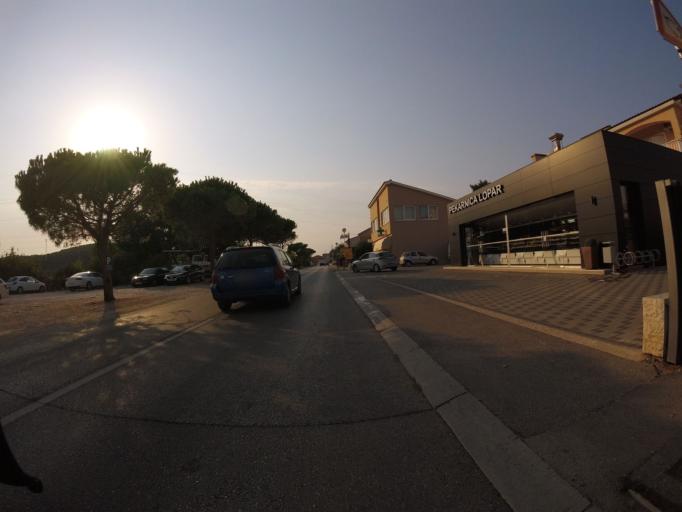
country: HR
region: Primorsko-Goranska
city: Lopar
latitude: 44.8287
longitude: 14.7334
